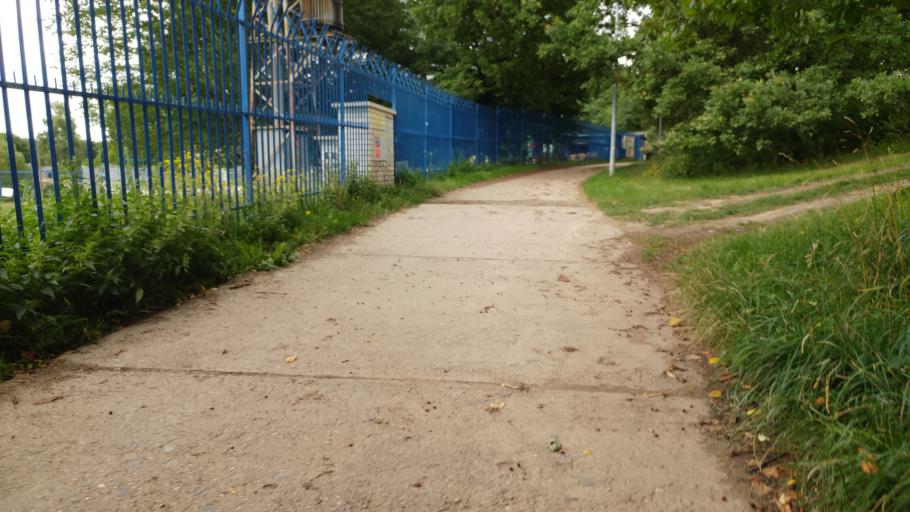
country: CZ
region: Central Bohemia
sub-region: Okres Praha-Zapad
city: Pruhonice
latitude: 50.0406
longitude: 14.5323
